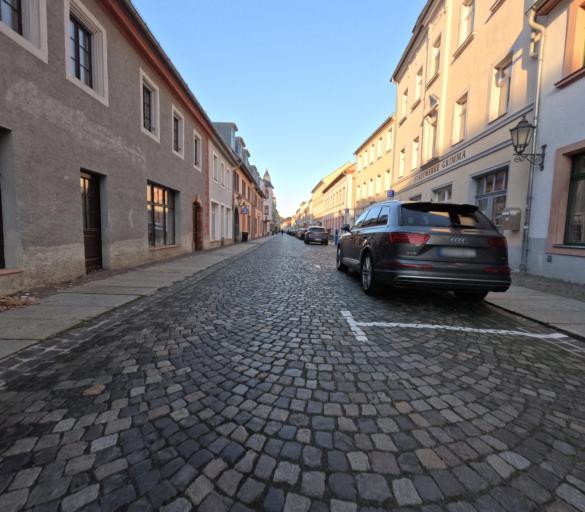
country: DE
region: Saxony
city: Grimma
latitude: 51.2337
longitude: 12.7269
